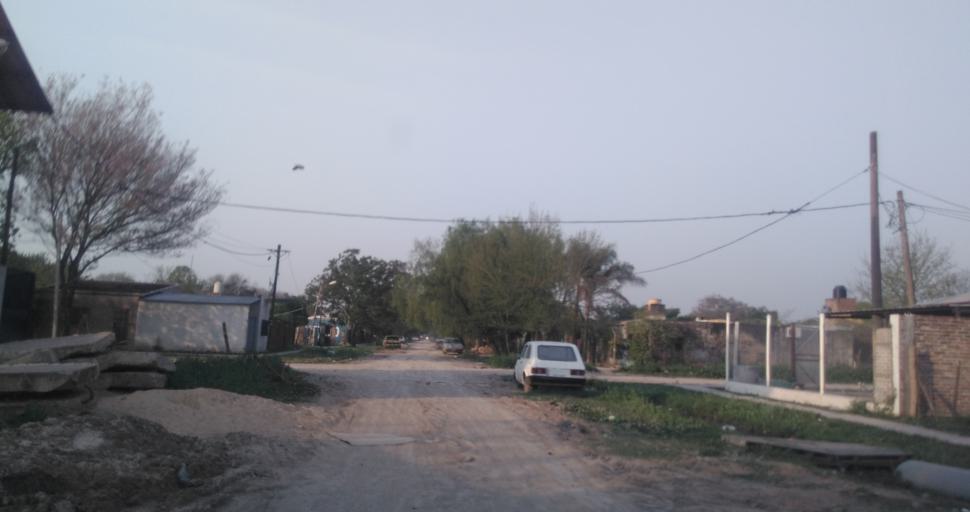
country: AR
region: Chaco
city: Resistencia
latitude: -27.4755
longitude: -59.0119
